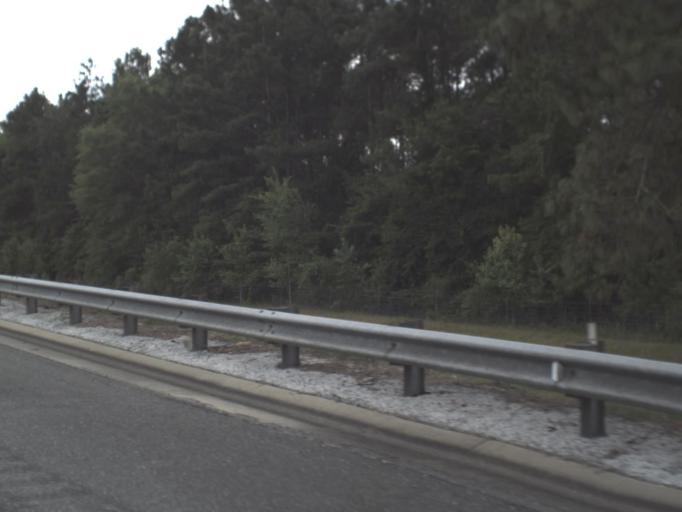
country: US
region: Florida
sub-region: Columbia County
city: Five Points
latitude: 30.2084
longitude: -82.7033
